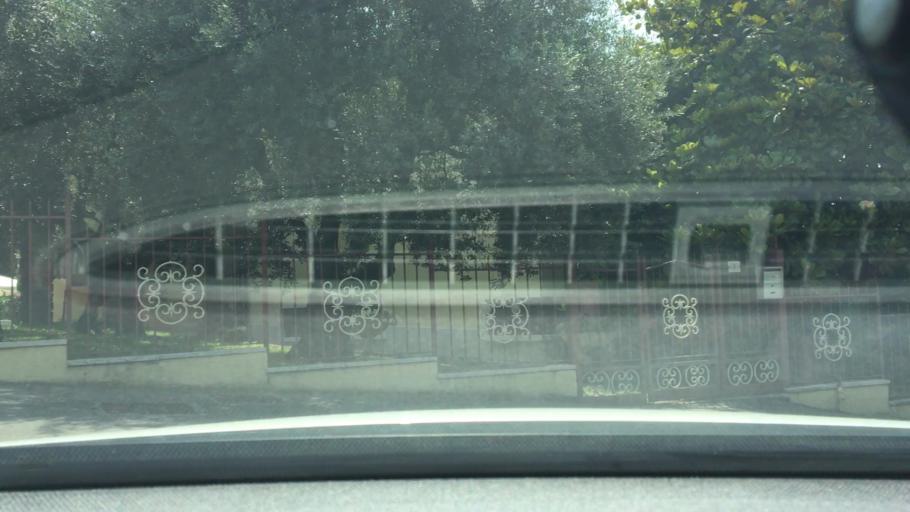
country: IT
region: Veneto
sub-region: Provincia di Verona
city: San Pietro
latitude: 45.4331
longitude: 11.1231
